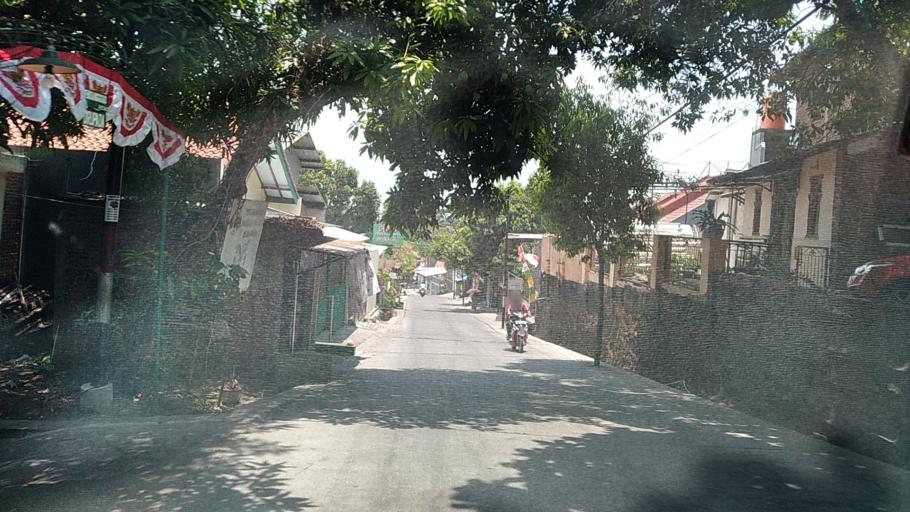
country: ID
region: Central Java
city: Semarang
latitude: -7.0119
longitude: 110.4548
